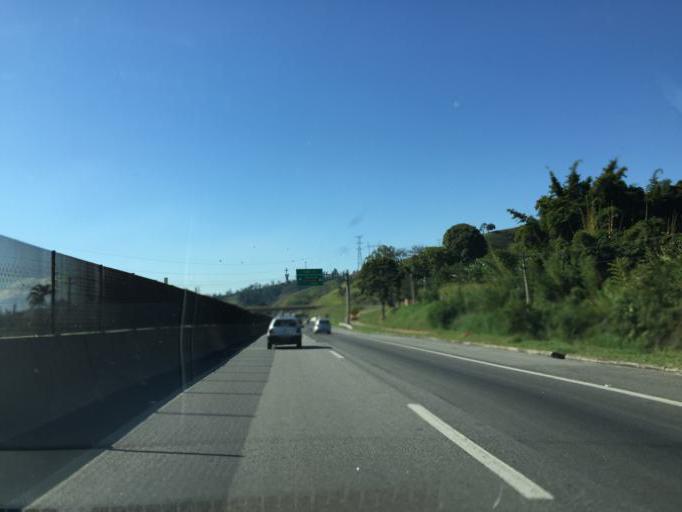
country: BR
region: Sao Paulo
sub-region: Aparecida
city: Aparecida
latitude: -22.8612
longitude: -45.2355
